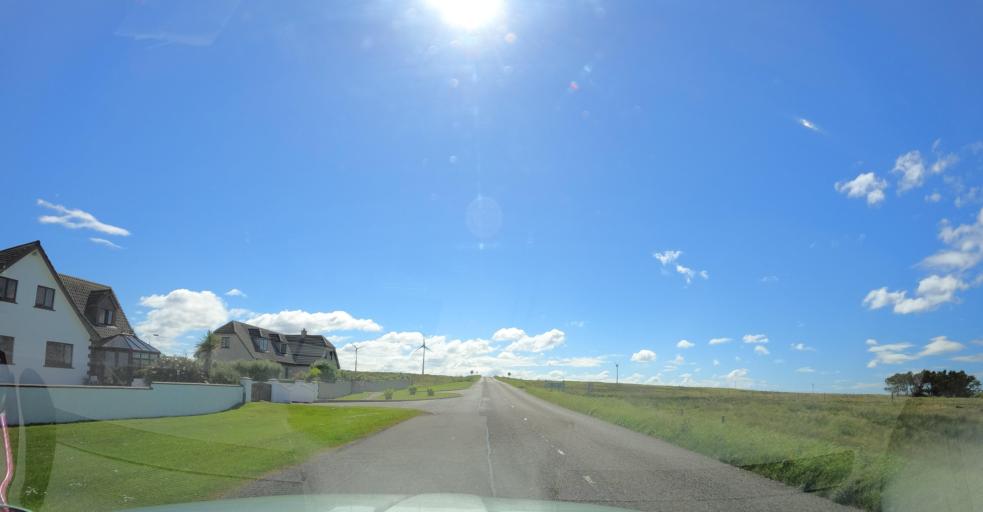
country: GB
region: Scotland
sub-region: Eilean Siar
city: Isle of Lewis
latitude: 58.3896
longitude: -6.4878
